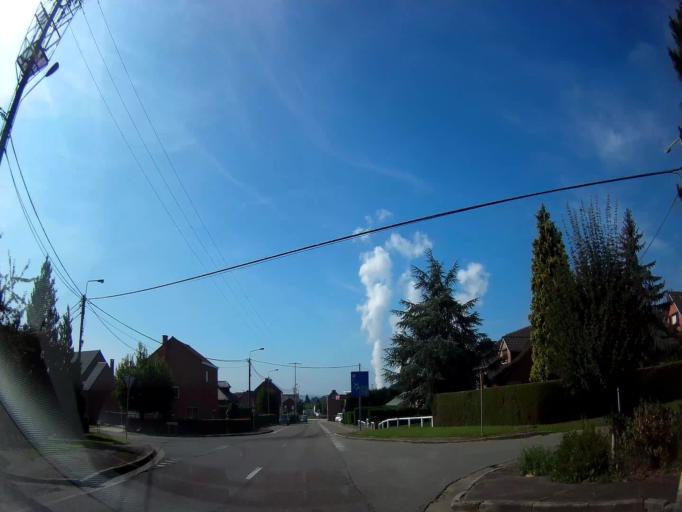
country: BE
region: Wallonia
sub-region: Province de Liege
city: Amay
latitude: 50.5611
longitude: 5.3069
